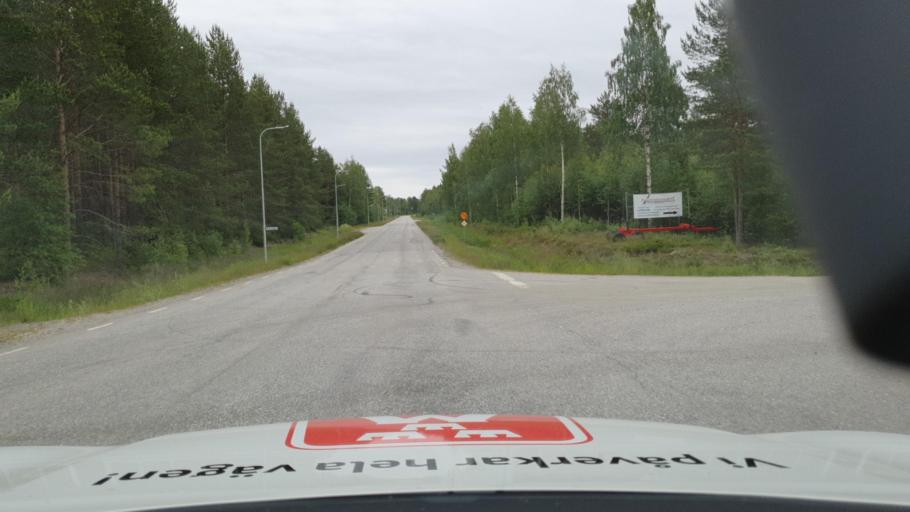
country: SE
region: Vaesterbotten
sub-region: Nordmalings Kommun
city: Nordmaling
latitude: 63.5483
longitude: 19.4217
